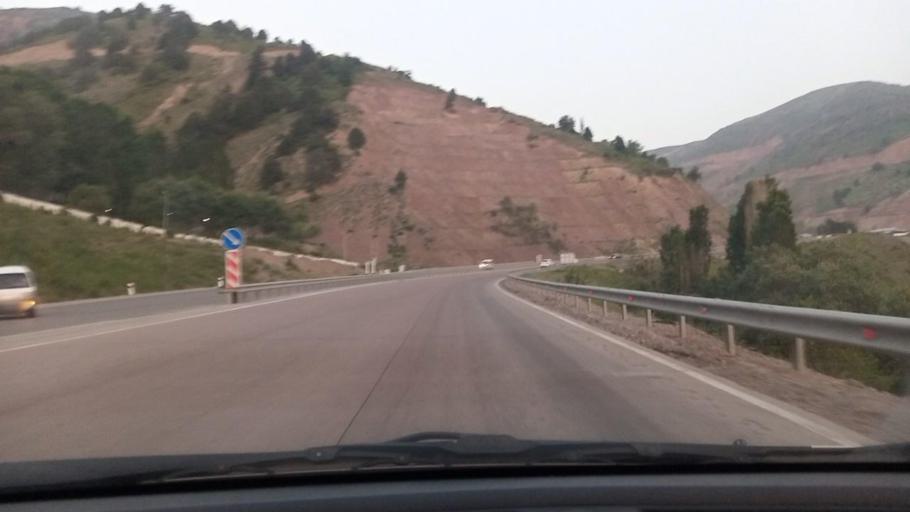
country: UZ
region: Toshkent
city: Angren
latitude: 41.1157
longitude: 70.4958
